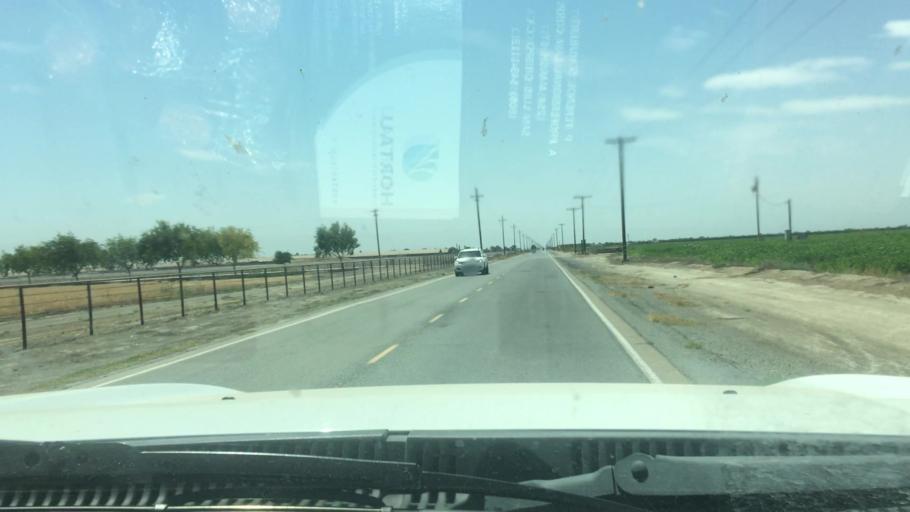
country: US
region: California
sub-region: Kings County
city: Corcoran
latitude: 36.0510
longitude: -119.4450
